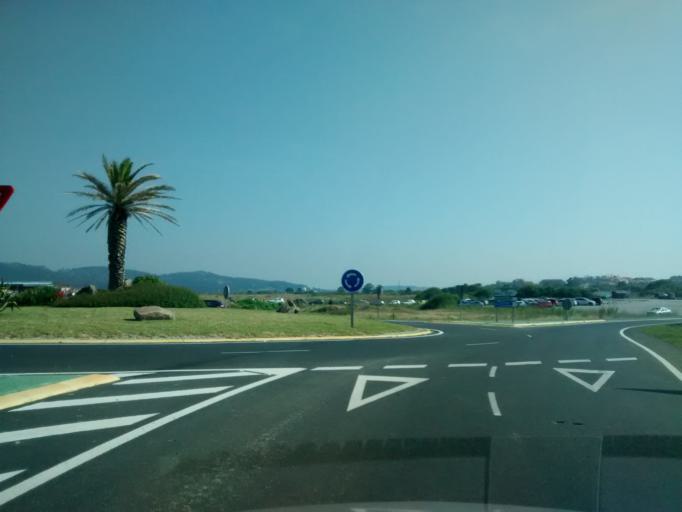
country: ES
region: Galicia
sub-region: Provincia de Pontevedra
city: O Grove
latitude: 42.4393
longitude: -8.8710
